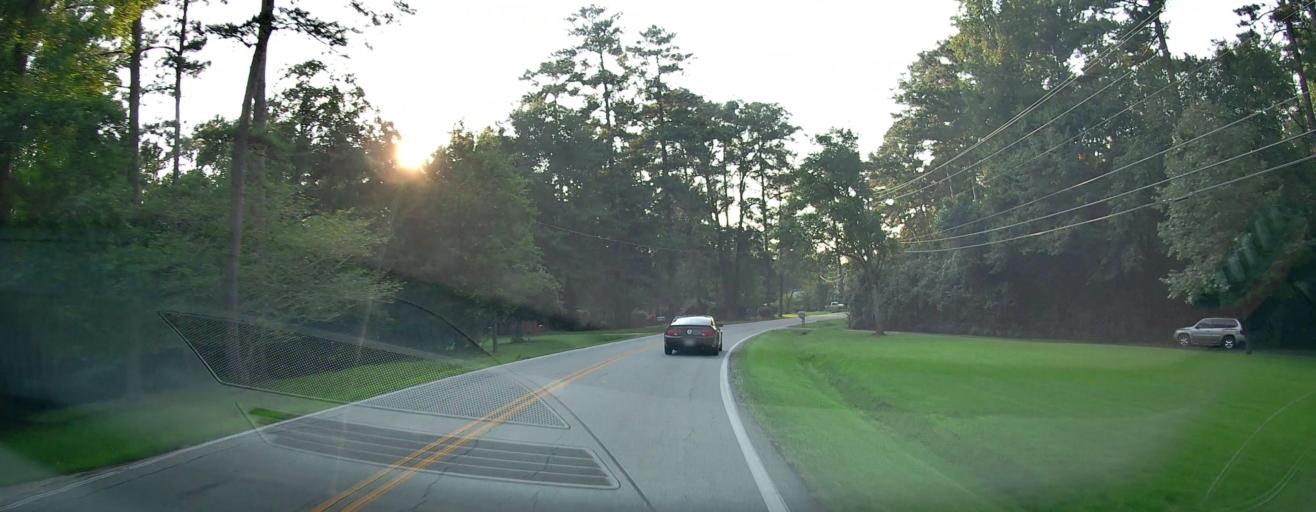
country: US
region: Georgia
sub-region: Bibb County
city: Macon
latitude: 32.9140
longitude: -83.7193
